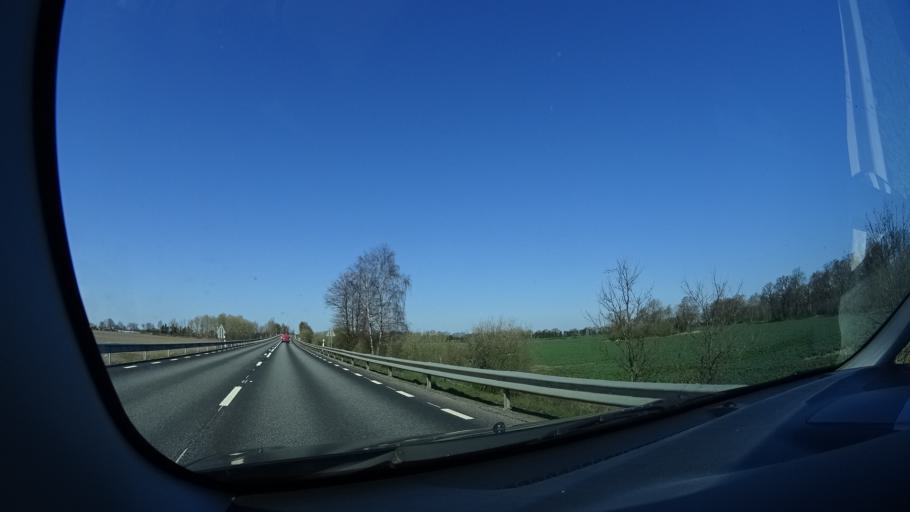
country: SE
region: Skane
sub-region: Angelholms Kommun
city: Strovelstorp
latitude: 56.2019
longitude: 12.7938
